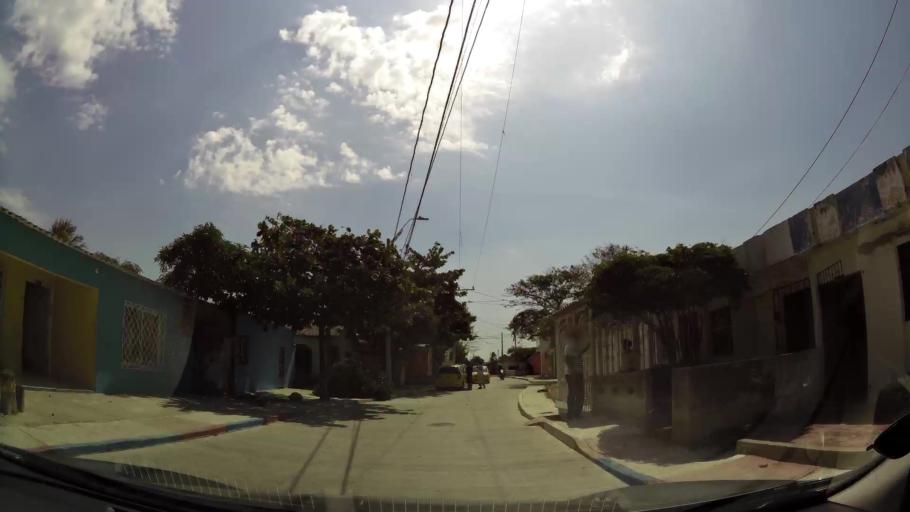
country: CO
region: Atlantico
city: Barranquilla
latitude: 10.9652
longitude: -74.8313
